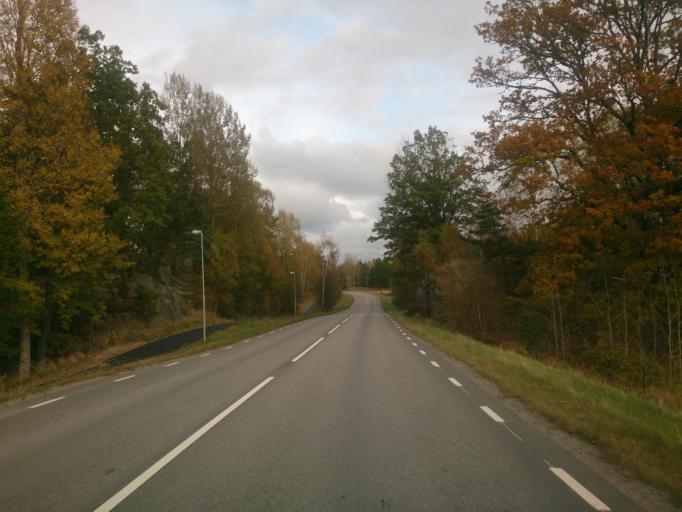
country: SE
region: OEstergoetland
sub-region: Atvidabergs Kommun
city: Atvidaberg
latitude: 58.2138
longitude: 16.0135
